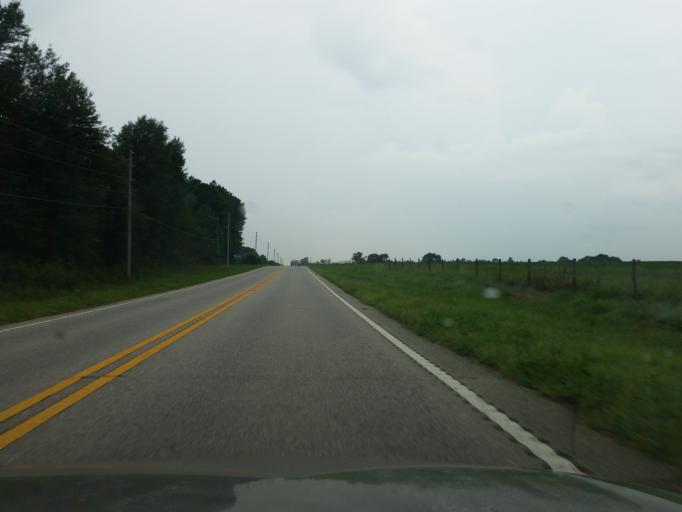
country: US
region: Alabama
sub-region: Baldwin County
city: Elberta
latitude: 30.5388
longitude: -87.5421
